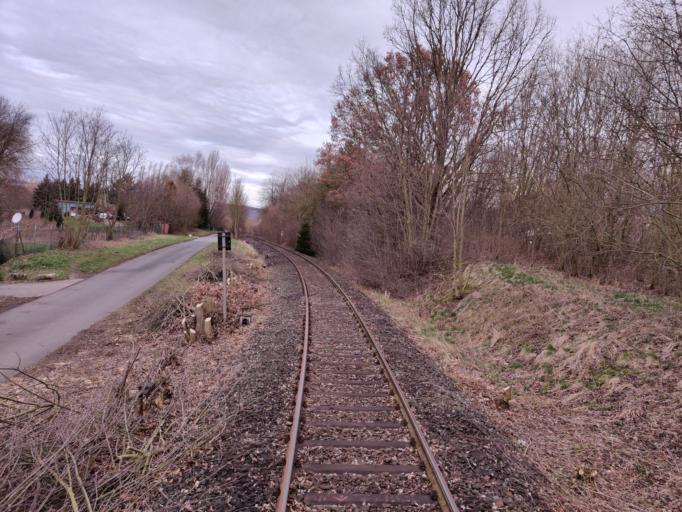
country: DE
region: Lower Saxony
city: Bockenem
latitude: 52.0171
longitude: 10.1242
